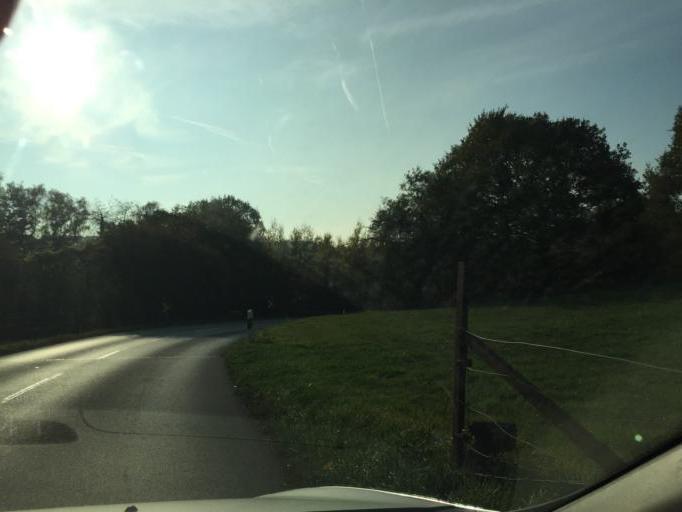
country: LU
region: Luxembourg
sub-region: Canton de Luxembourg
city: Contern
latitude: 49.5689
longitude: 6.2176
